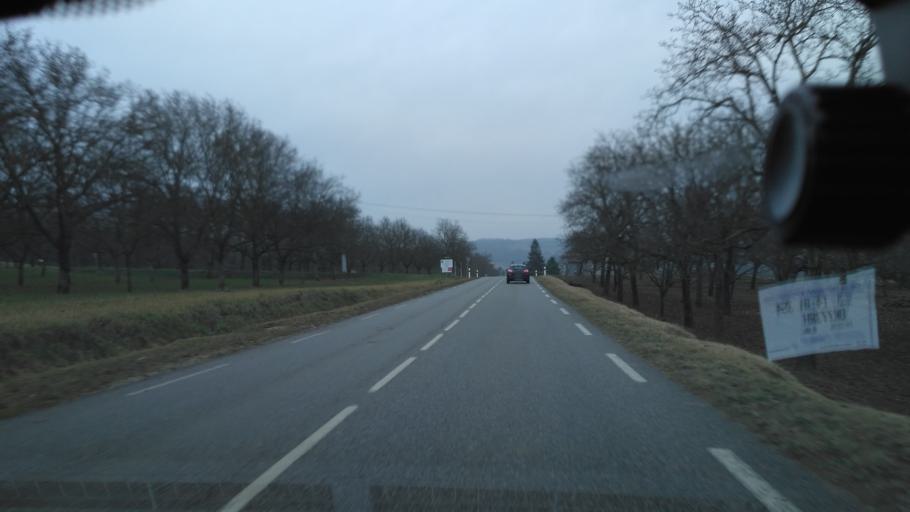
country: FR
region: Rhone-Alpes
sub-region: Departement de la Drome
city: Genissieux
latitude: 45.1387
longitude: 5.1161
